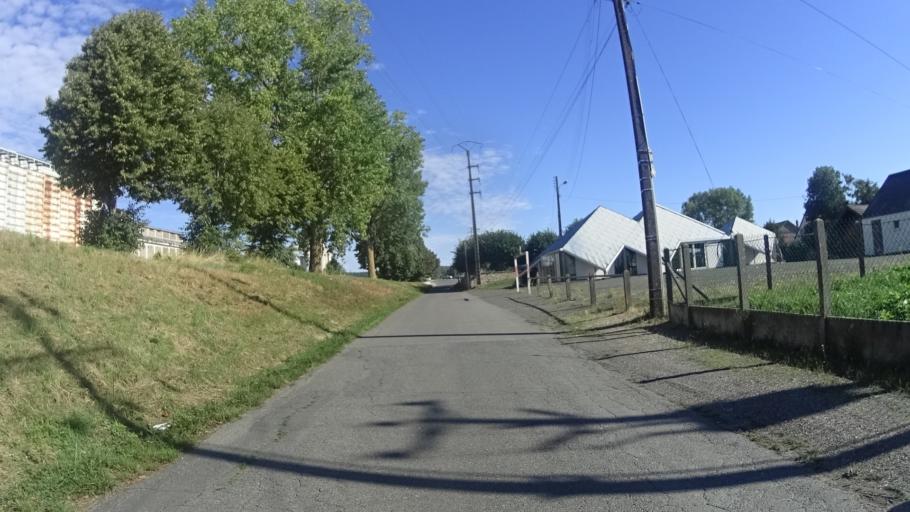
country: FR
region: Centre
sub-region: Departement du Cher
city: Saint-Satur
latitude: 47.3371
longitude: 2.8592
